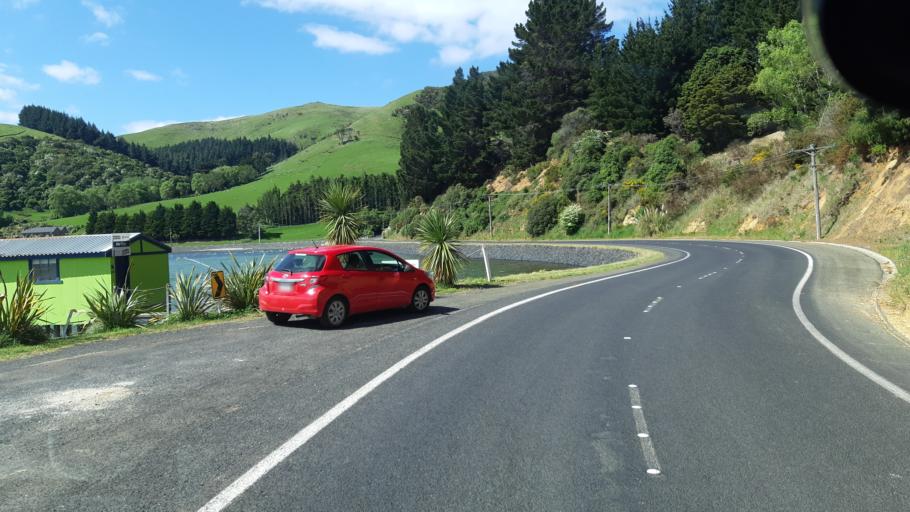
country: NZ
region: Otago
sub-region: Dunedin City
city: Portobello
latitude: -45.8339
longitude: 170.6696
